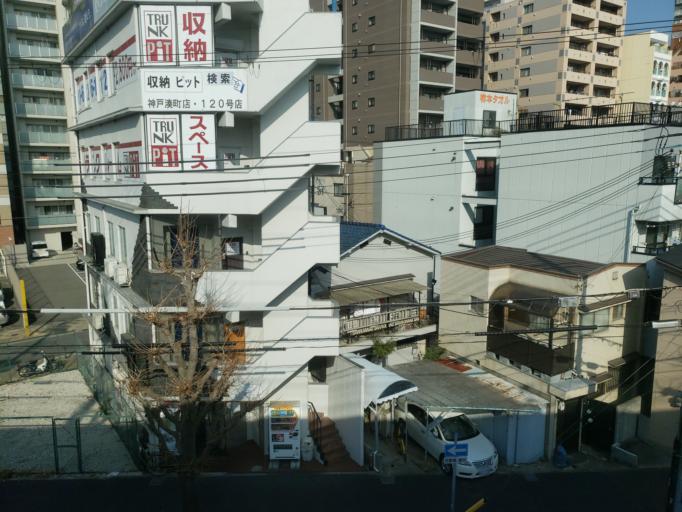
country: JP
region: Hyogo
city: Kobe
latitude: 34.6746
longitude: 135.1754
